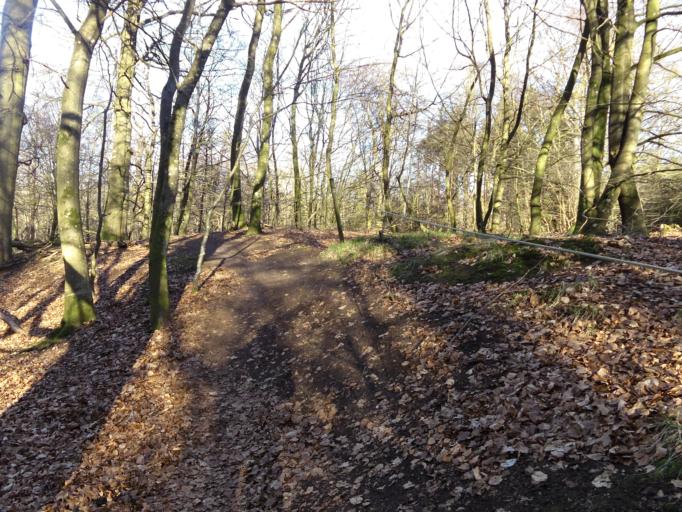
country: DK
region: South Denmark
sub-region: Haderslev Kommune
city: Gram
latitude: 55.2918
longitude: 9.0672
